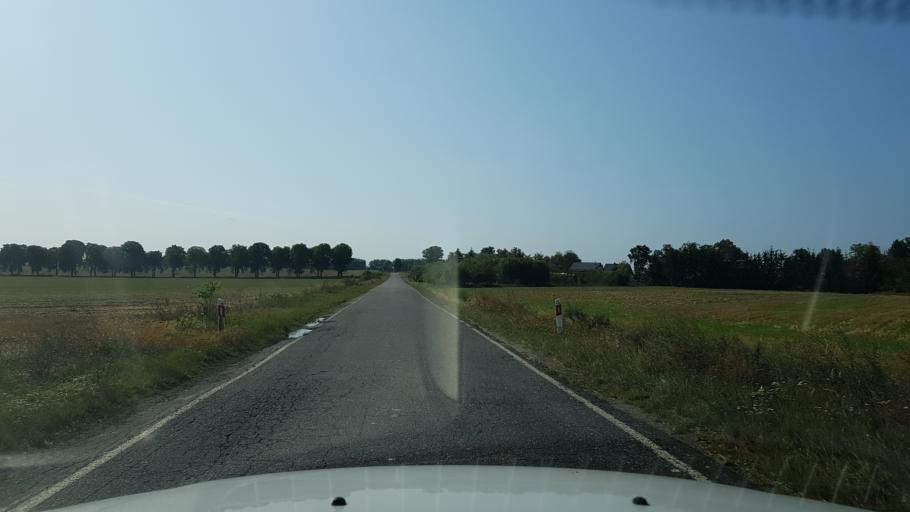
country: PL
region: West Pomeranian Voivodeship
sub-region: Powiat stargardzki
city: Dolice
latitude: 53.1484
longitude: 15.2420
